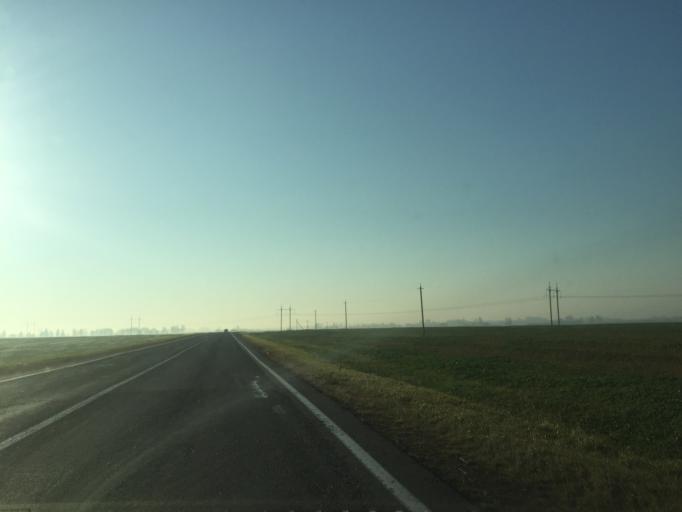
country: BY
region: Gomel
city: Buda-Kashalyova
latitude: 52.8295
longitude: 30.7140
